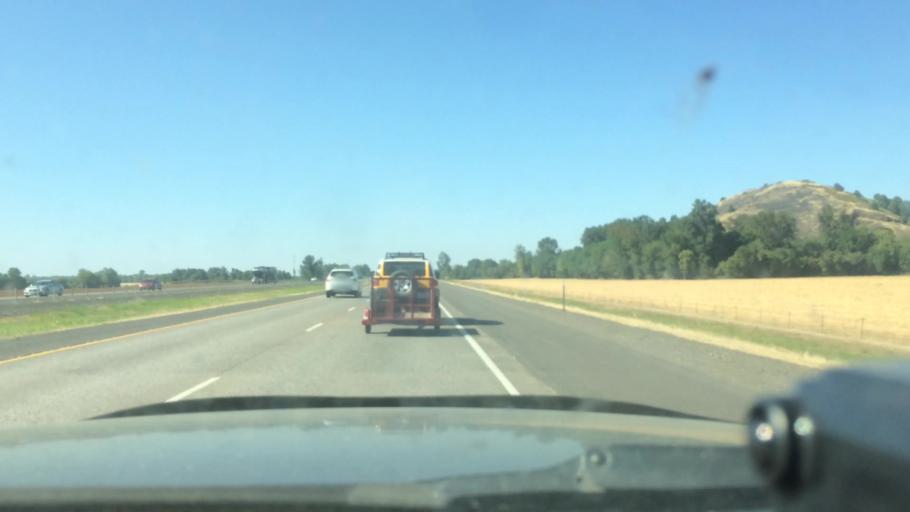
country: US
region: Oregon
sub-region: Linn County
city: Brownsville
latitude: 44.4458
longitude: -123.0606
